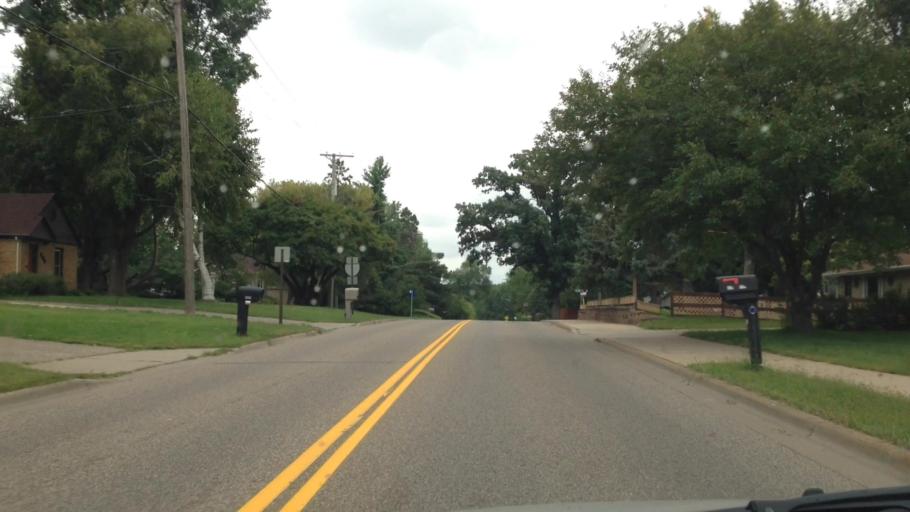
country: US
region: Minnesota
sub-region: Hennepin County
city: Saint Louis Park
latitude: 44.9750
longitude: -93.3809
